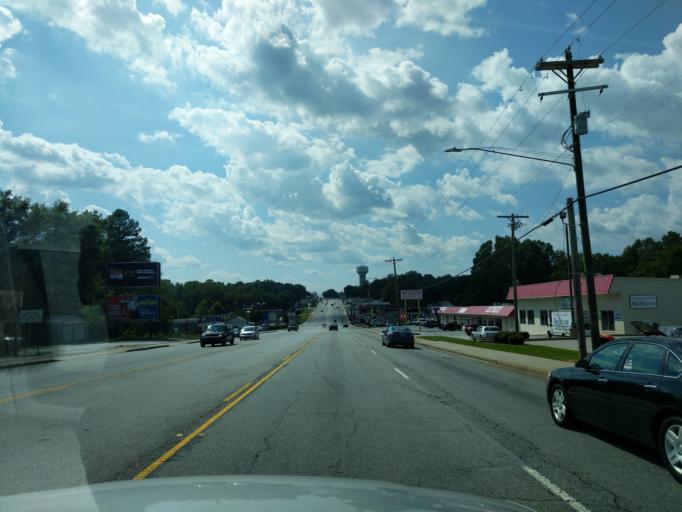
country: US
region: South Carolina
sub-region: Pickens County
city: Easley
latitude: 34.8210
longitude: -82.5905
